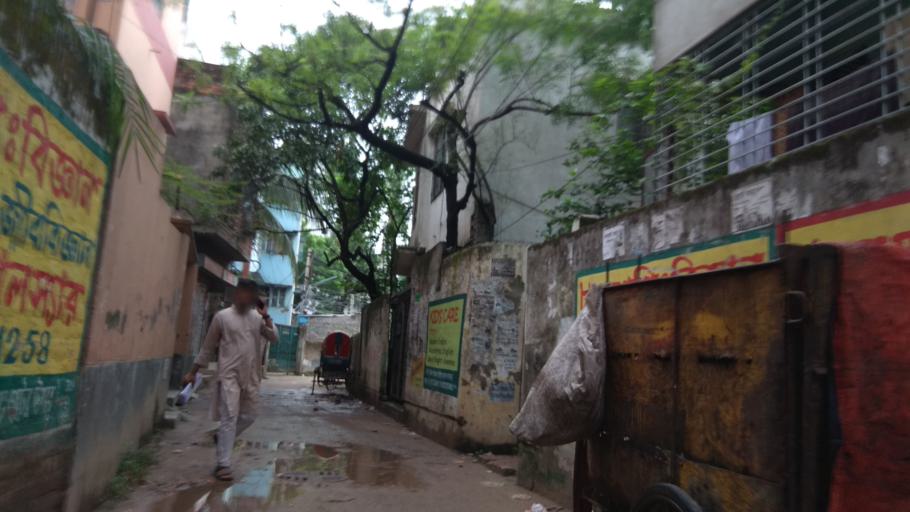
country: BD
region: Dhaka
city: Azimpur
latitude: 23.7988
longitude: 90.3680
